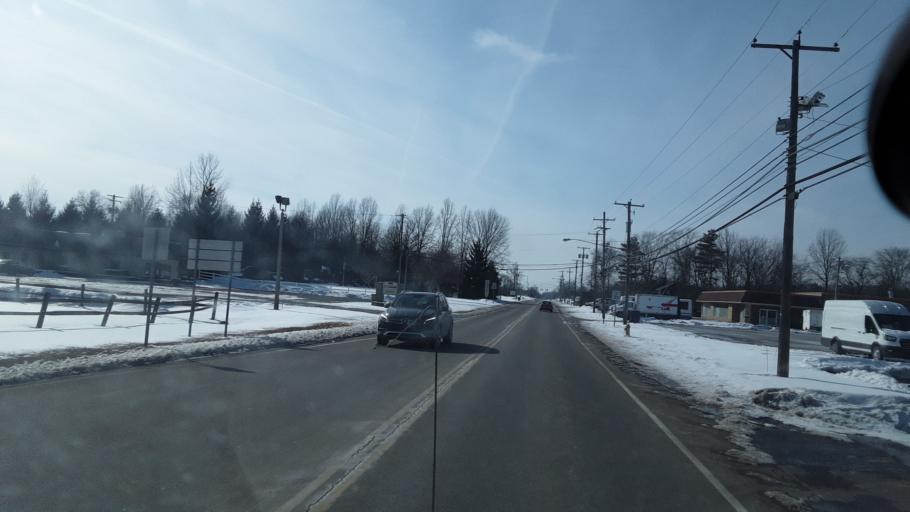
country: US
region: Ohio
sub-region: Mahoning County
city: Canfield
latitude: 41.0248
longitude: -80.7817
